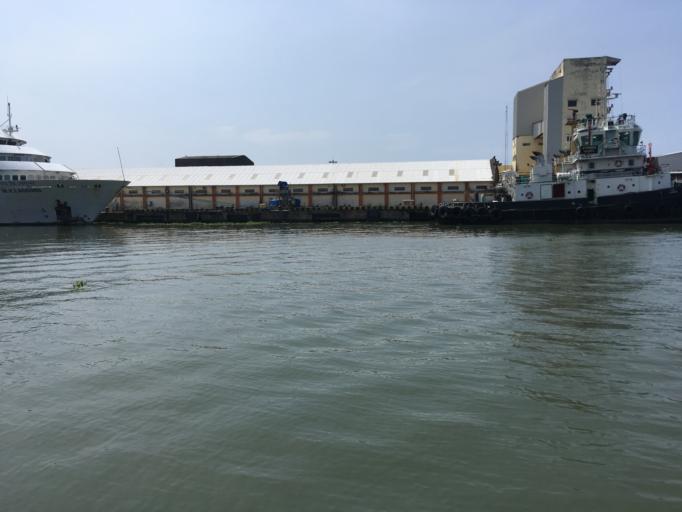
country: IN
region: Kerala
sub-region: Ernakulam
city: Cochin
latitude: 9.9698
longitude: 76.2646
